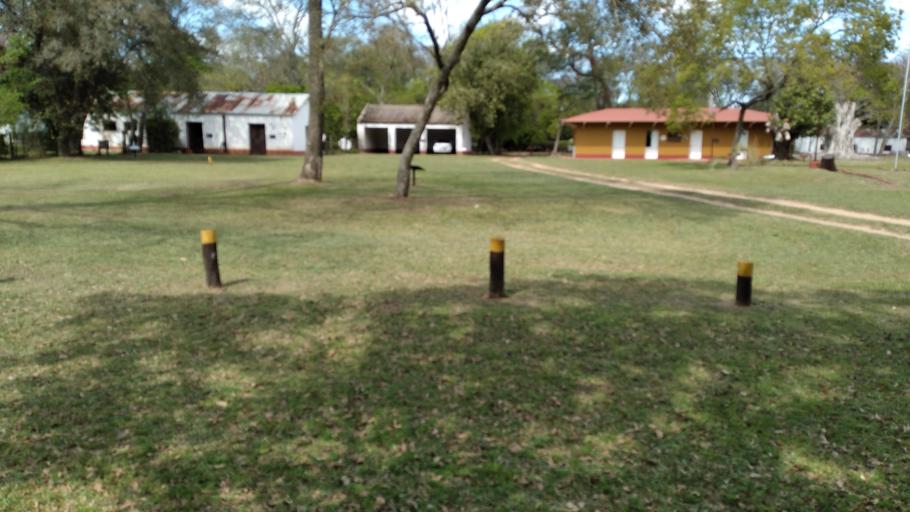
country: AR
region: Corrientes
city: Palmar Grande
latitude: -28.0176
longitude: -58.0286
